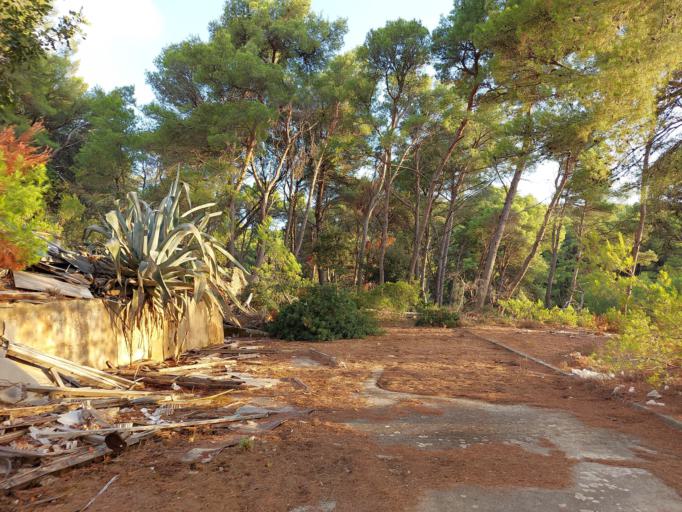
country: HR
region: Dubrovacko-Neretvanska
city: Smokvica
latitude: 42.7373
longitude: 16.8287
